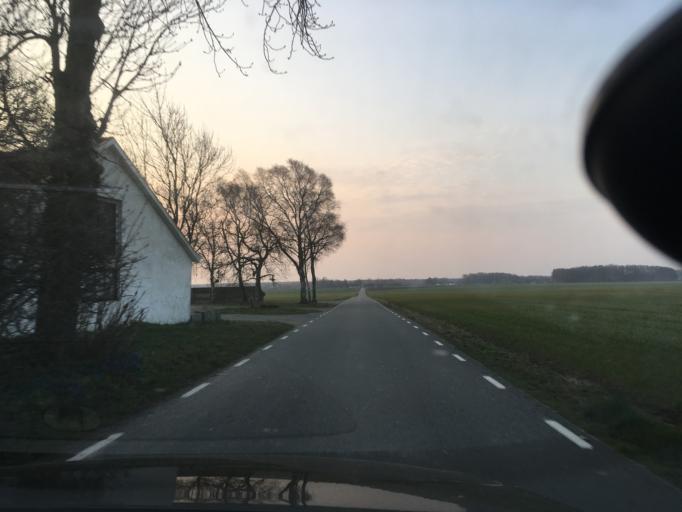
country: SE
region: Skane
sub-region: Ystads Kommun
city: Kopingebro
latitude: 55.4093
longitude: 14.1543
